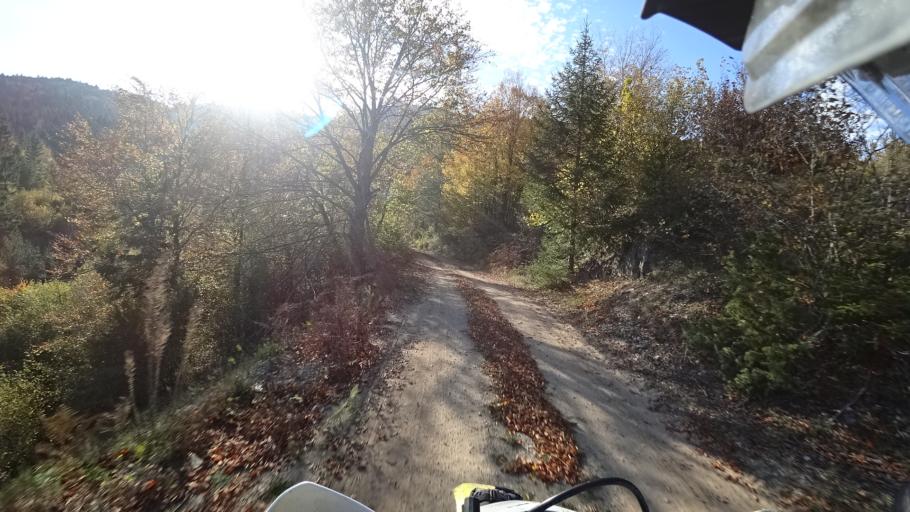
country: HR
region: Karlovacka
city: Plaski
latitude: 44.9995
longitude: 15.4067
